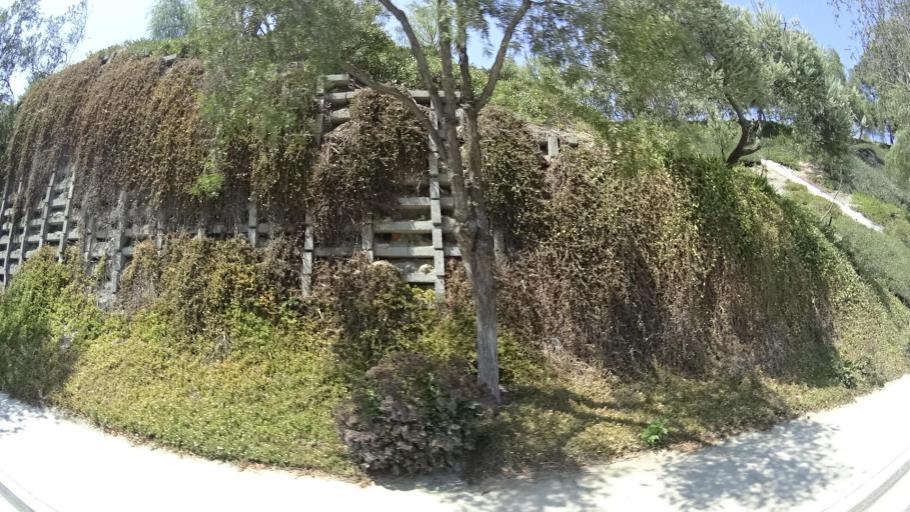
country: US
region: California
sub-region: San Diego County
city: Vista
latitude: 33.2257
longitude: -117.2639
